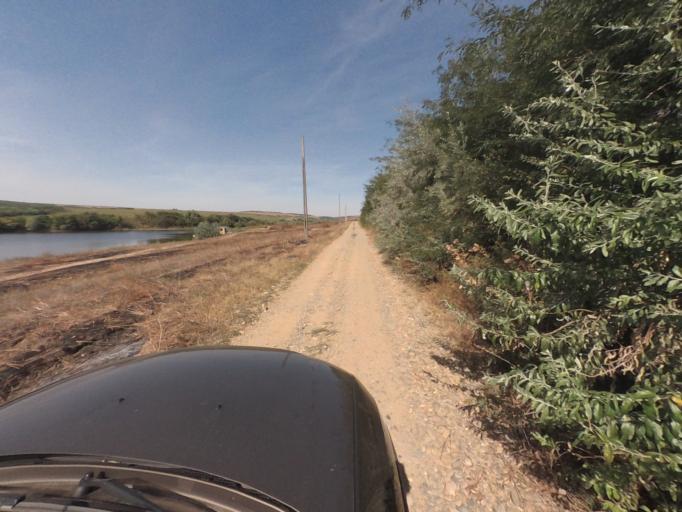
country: RO
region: Vaslui
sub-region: Comuna Costesti
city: Costesti
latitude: 46.5239
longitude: 27.7391
